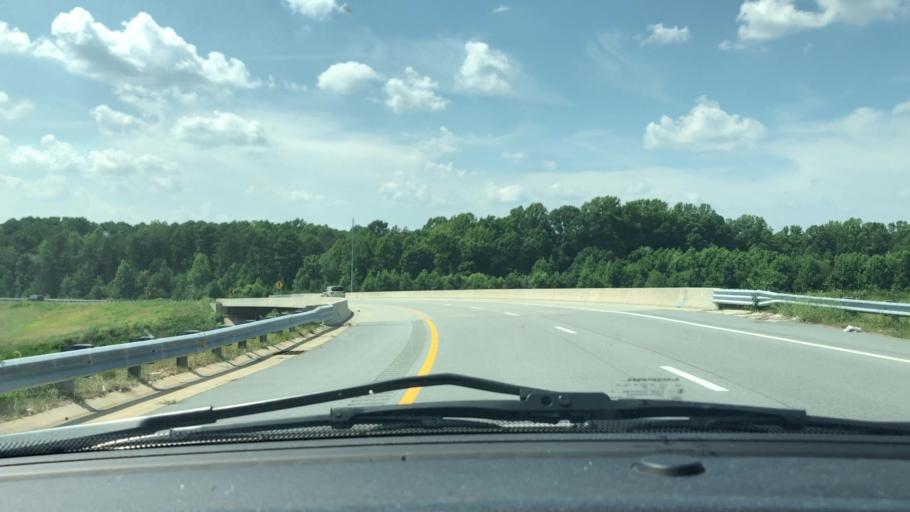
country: US
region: North Carolina
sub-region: Guilford County
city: Summerfield
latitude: 36.1184
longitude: -79.9061
